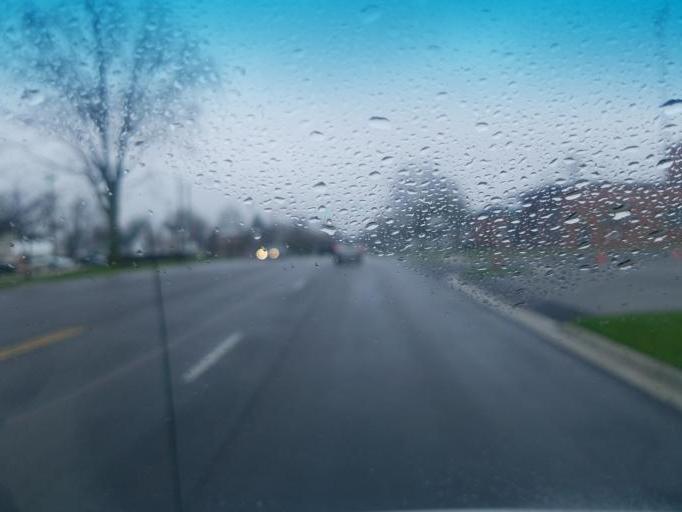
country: US
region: Ohio
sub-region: Hancock County
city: Findlay
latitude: 41.0728
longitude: -83.6498
